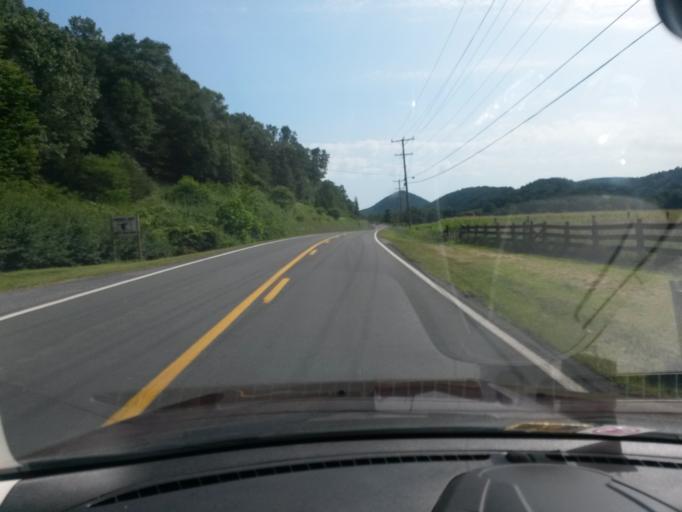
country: US
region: West Virginia
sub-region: Hardy County
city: Moorefield
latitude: 39.0345
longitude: -78.7512
